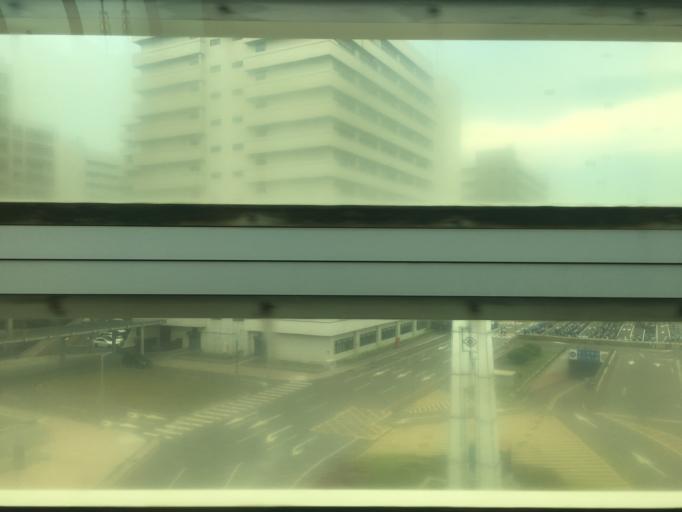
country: TW
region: Taiwan
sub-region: Taoyuan
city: Taoyuan
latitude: 25.0620
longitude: 121.3696
